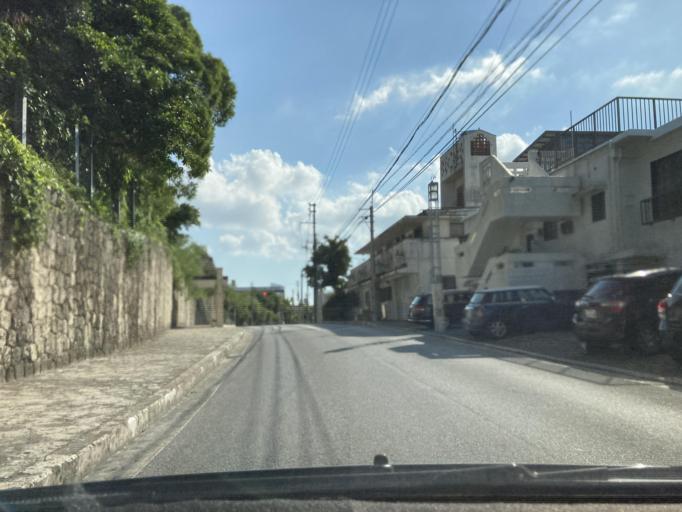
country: JP
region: Okinawa
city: Naha-shi
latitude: 26.2161
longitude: 127.7181
